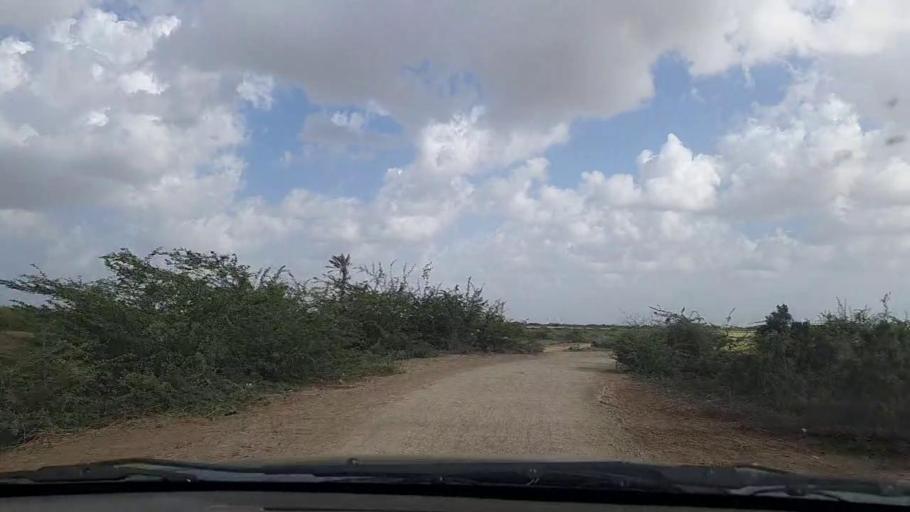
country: PK
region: Sindh
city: Keti Bandar
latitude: 24.0872
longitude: 67.6161
